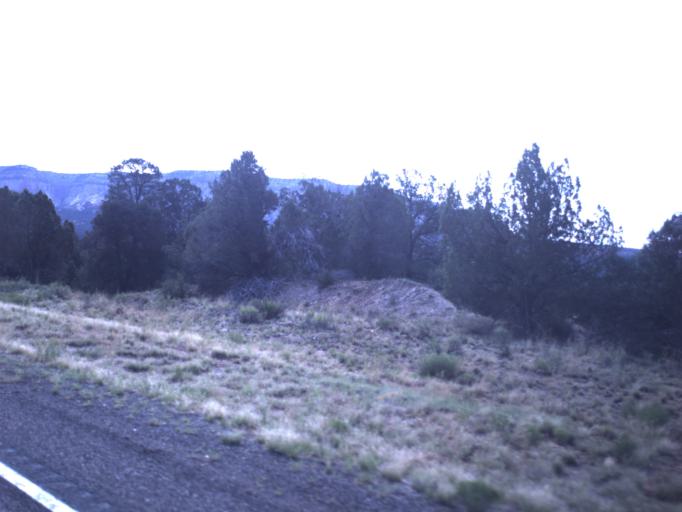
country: US
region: Utah
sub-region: Kane County
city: Kanab
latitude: 37.2197
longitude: -112.6958
